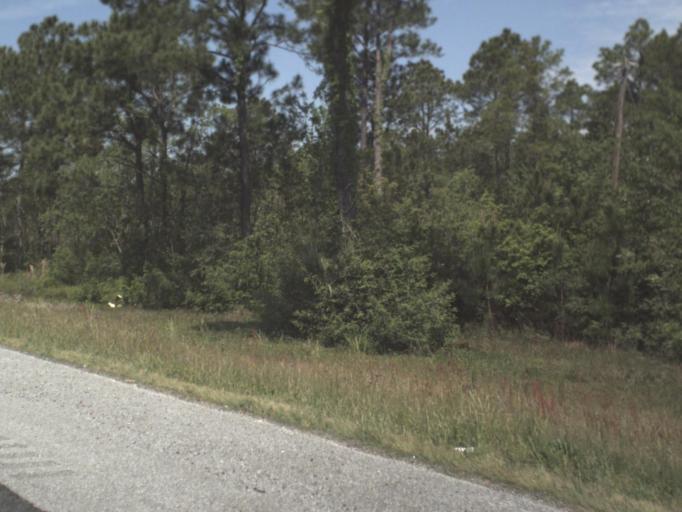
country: US
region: Florida
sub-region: Santa Rosa County
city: Pace
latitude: 30.5342
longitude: -87.1058
